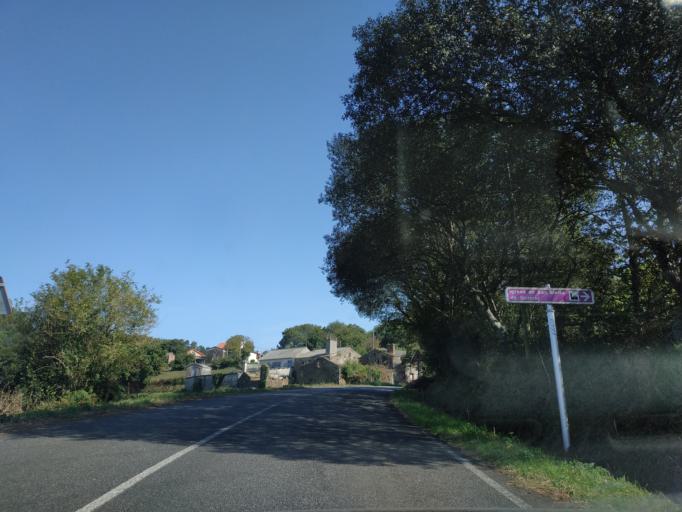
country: ES
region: Galicia
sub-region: Provincia da Coruna
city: Laracha
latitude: 43.2264
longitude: -8.5446
